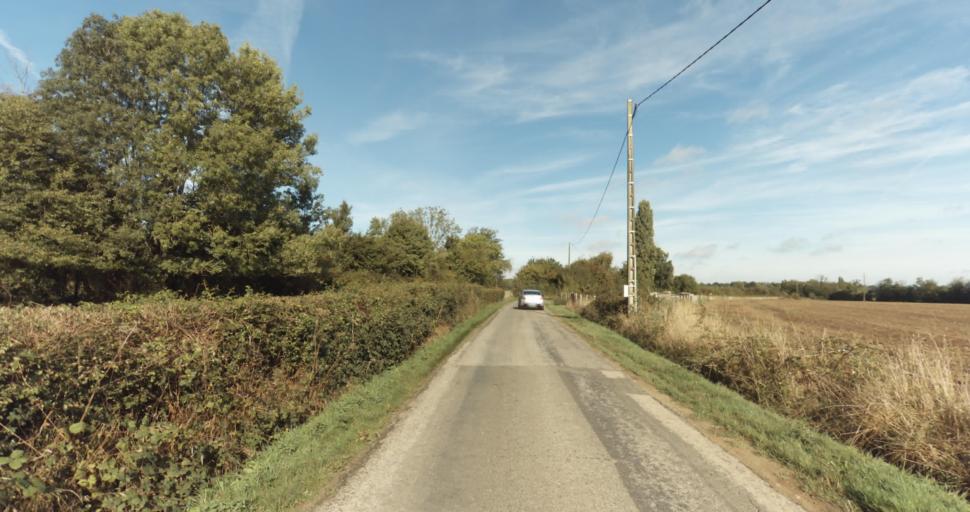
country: FR
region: Lower Normandy
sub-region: Departement de l'Orne
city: Vimoutiers
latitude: 48.9187
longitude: 0.2987
